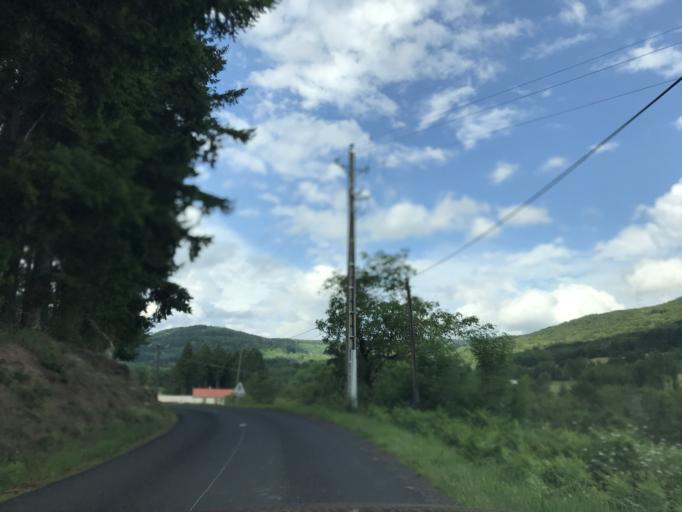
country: FR
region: Auvergne
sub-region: Departement du Puy-de-Dome
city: Celles-sur-Durolle
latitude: 45.8140
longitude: 3.6143
